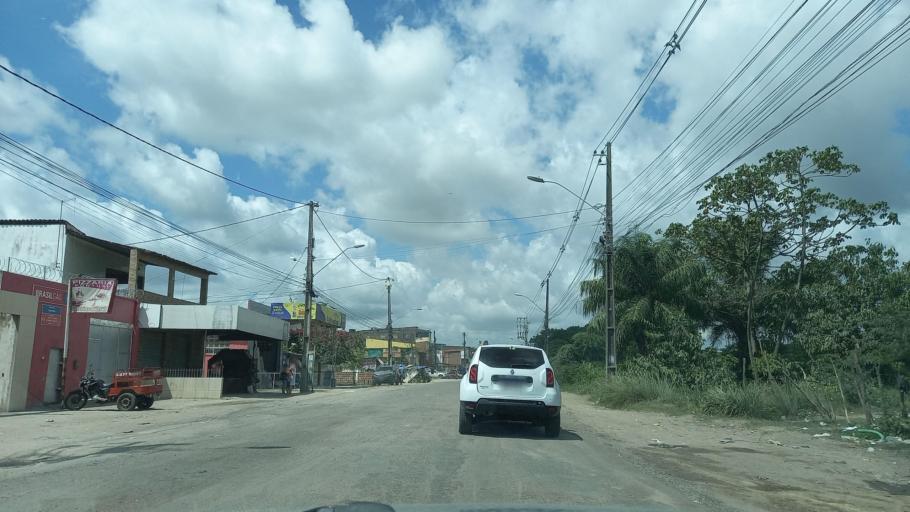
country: BR
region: Pernambuco
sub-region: Jaboatao Dos Guararapes
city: Jaboatao
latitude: -8.1572
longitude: -34.9696
